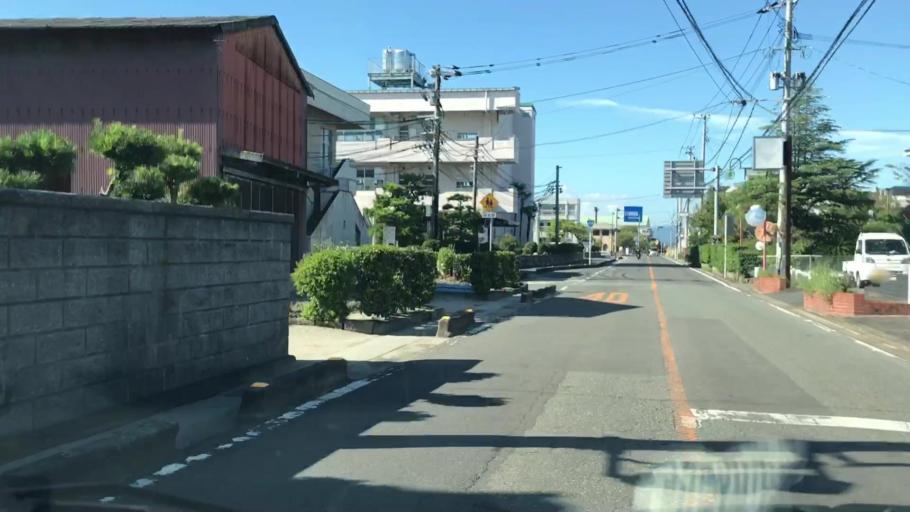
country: JP
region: Saga Prefecture
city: Okawa
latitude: 33.1897
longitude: 130.3195
